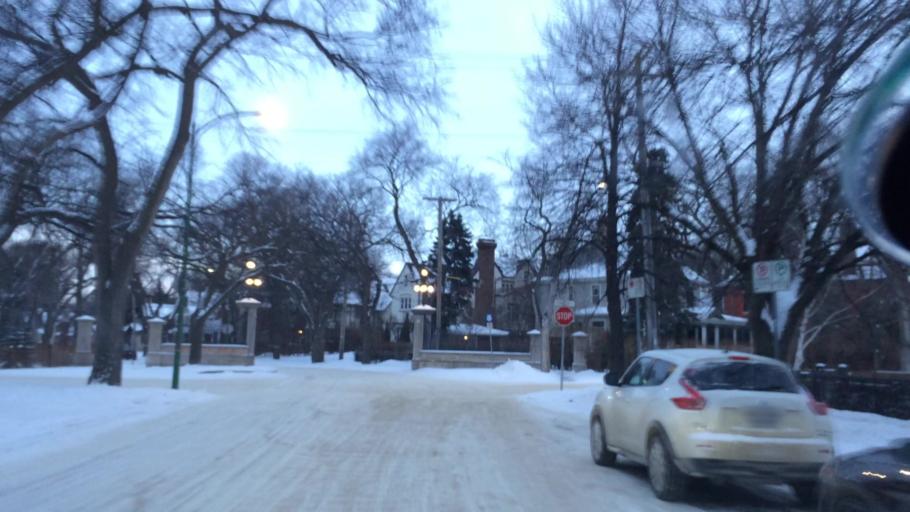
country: CA
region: Manitoba
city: Winnipeg
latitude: 49.8793
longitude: -97.1583
